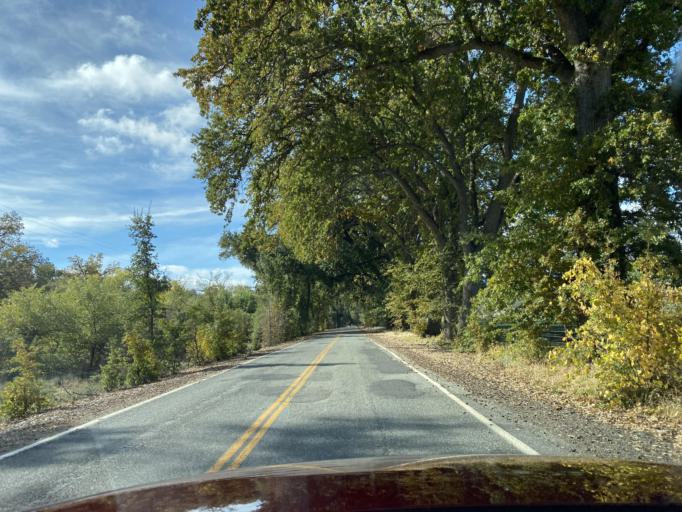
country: US
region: California
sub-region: Glenn County
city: Willows
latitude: 39.4169
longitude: -122.5386
